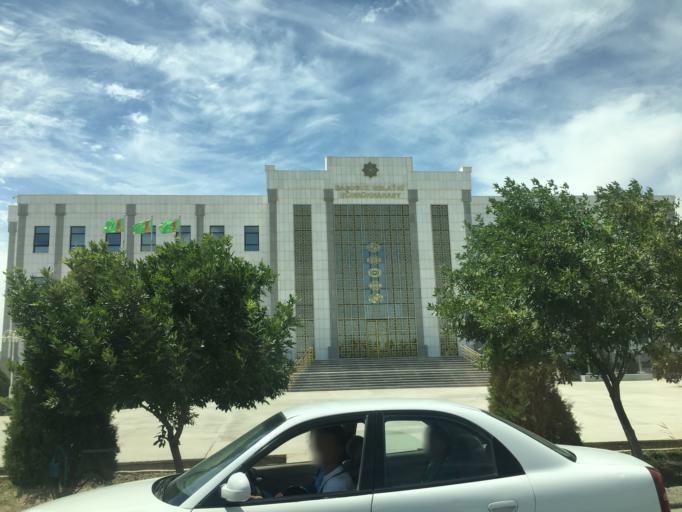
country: TM
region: Dasoguz
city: Dasoguz
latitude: 41.8280
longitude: 59.9439
